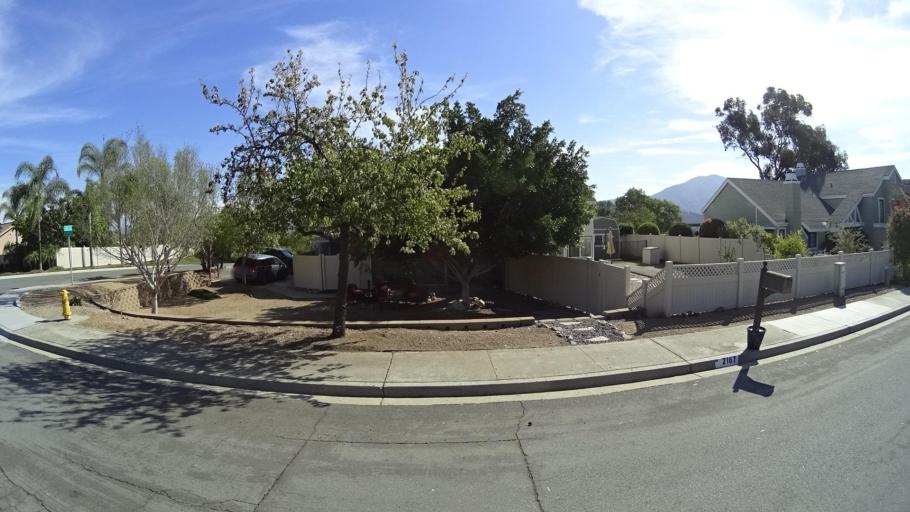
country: US
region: California
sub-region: San Diego County
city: Spring Valley
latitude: 32.7293
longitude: -116.9879
